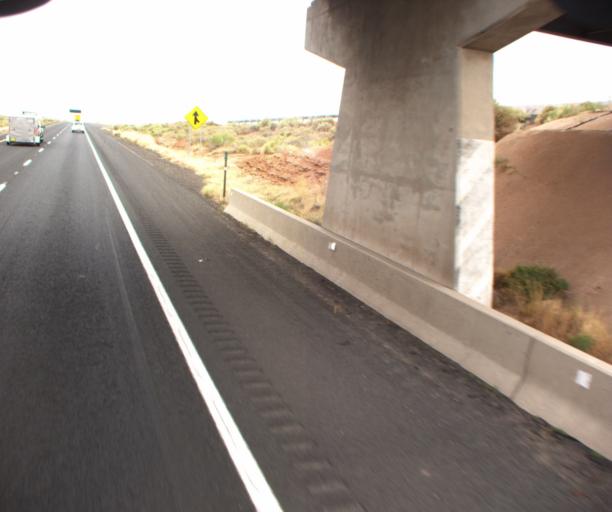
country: US
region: Arizona
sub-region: Navajo County
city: Joseph City
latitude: 34.9227
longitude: -110.2606
